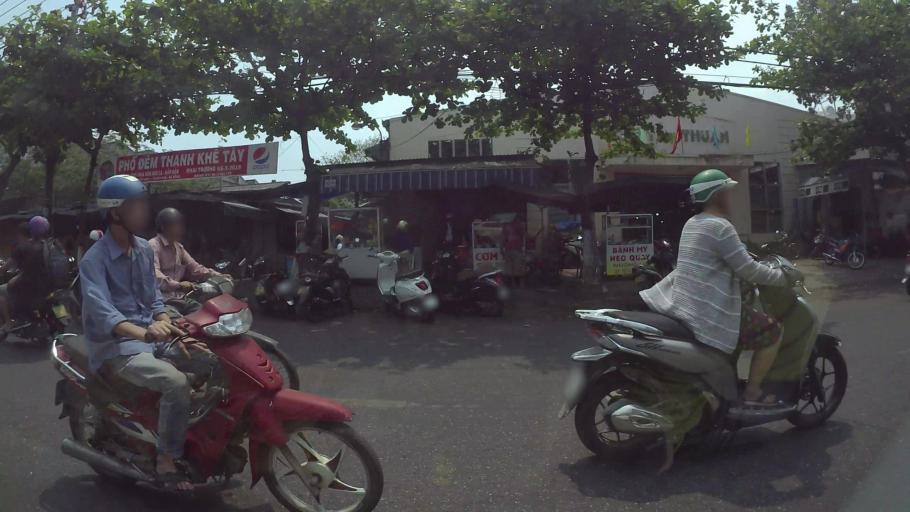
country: VN
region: Da Nang
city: Thanh Khe
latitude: 16.0718
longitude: 108.2053
